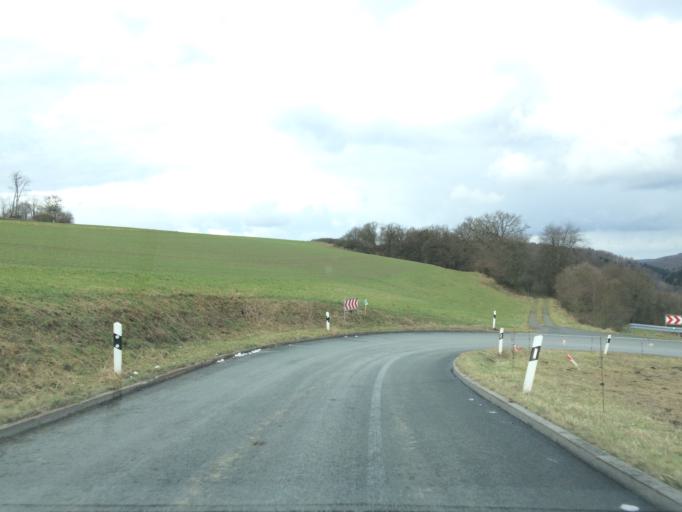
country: DE
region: Hesse
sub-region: Regierungsbezirk Darmstadt
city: Gravenwiesbach
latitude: 50.3832
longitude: 8.4049
